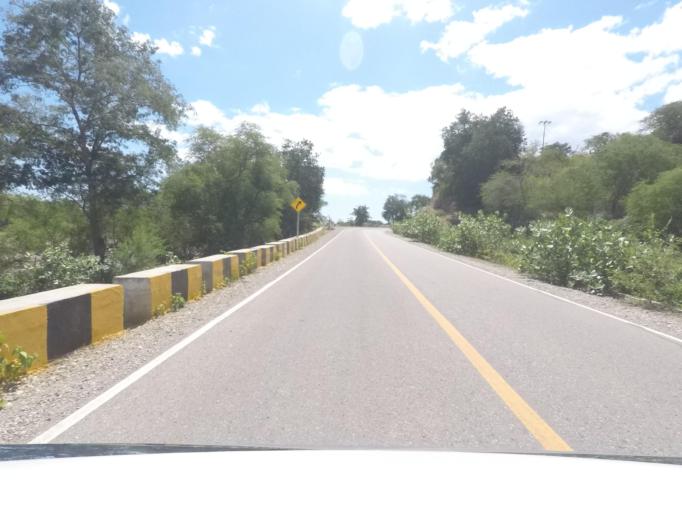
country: TL
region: Lautem
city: Lospalos
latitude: -8.3730
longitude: 126.8929
